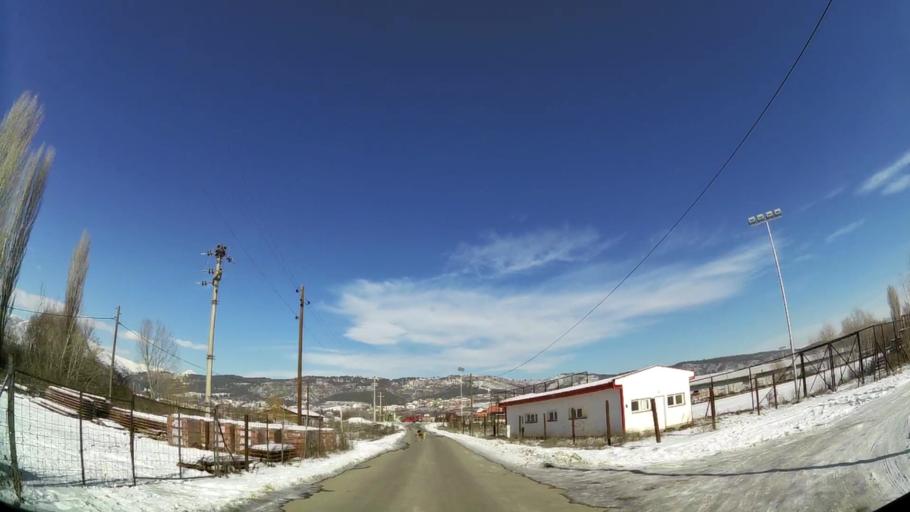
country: MK
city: Ljubin
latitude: 42.0040
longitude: 21.3092
